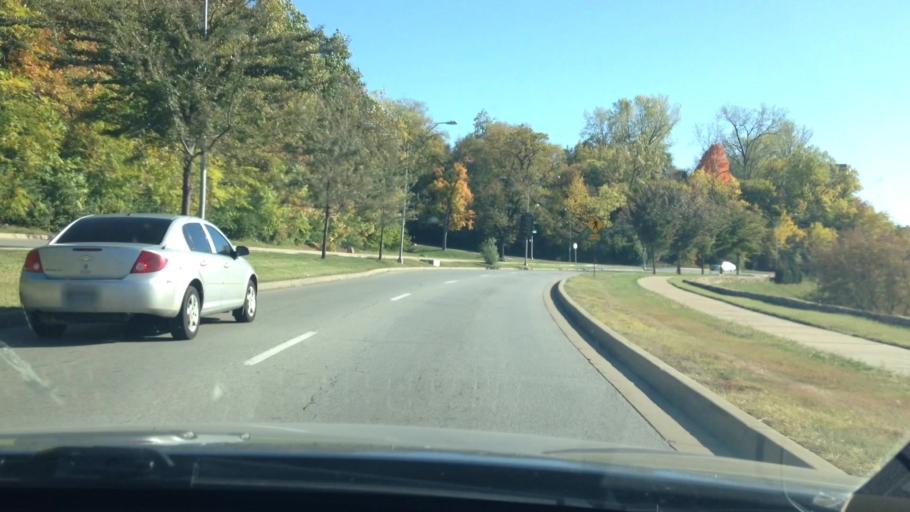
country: US
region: Missouri
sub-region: Jackson County
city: Kansas City
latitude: 39.0761
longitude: -94.5902
